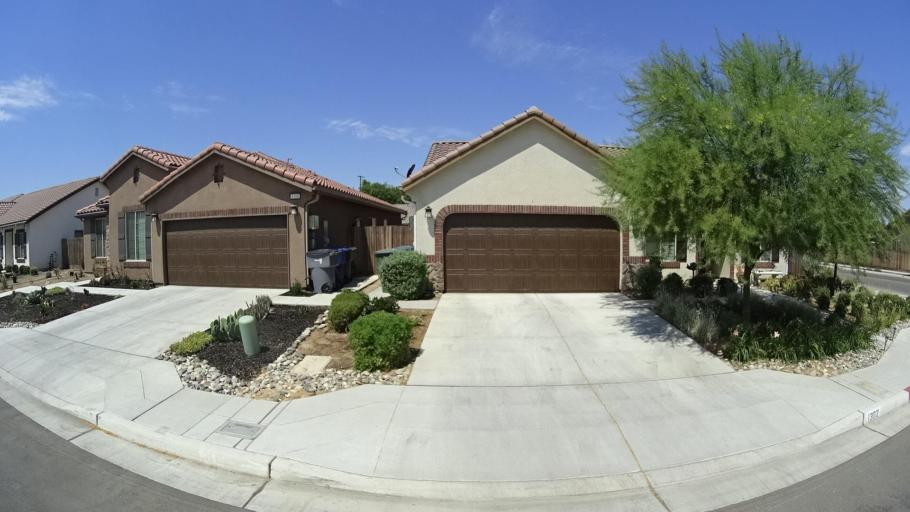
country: US
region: California
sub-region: Fresno County
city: Sunnyside
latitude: 36.7298
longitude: -119.7130
